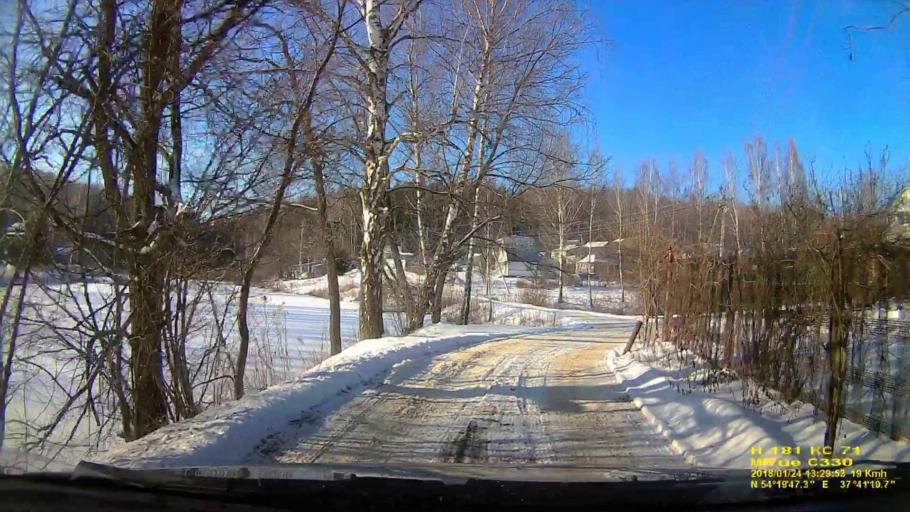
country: RU
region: Tula
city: Revyakino
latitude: 54.3299
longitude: 37.6887
